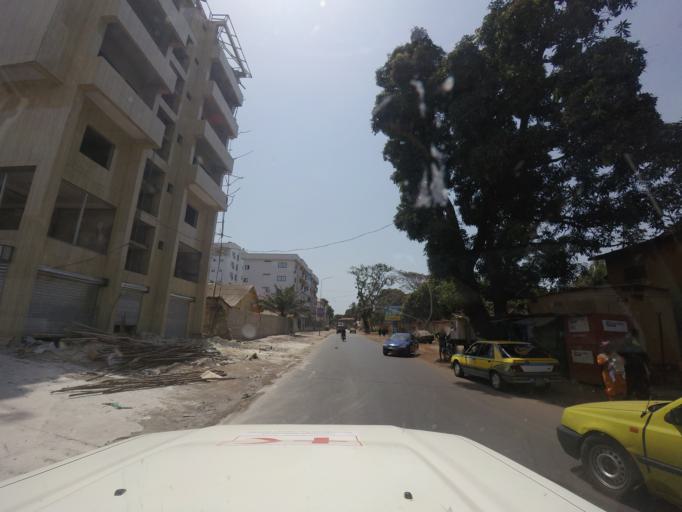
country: GN
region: Conakry
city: Camayenne
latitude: 9.5179
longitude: -13.7020
